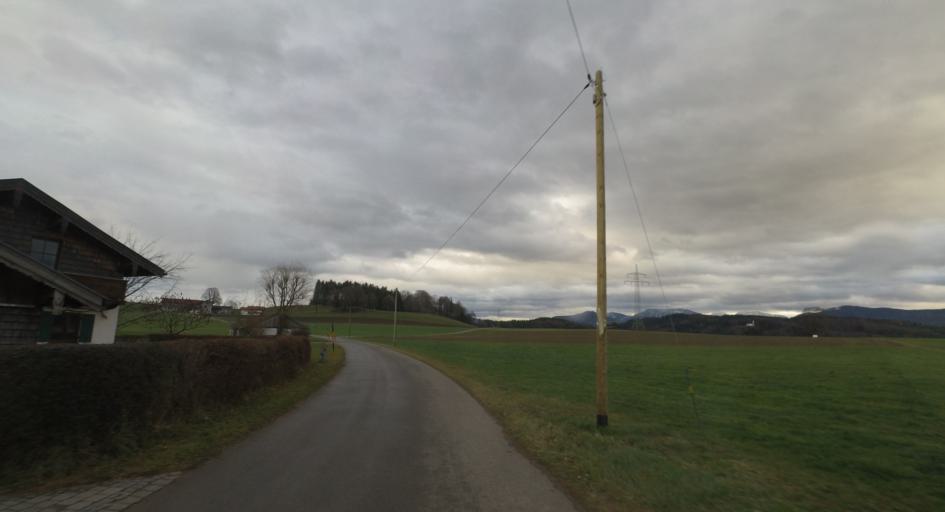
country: DE
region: Bavaria
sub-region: Upper Bavaria
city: Vachendorf
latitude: 47.8514
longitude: 12.6059
